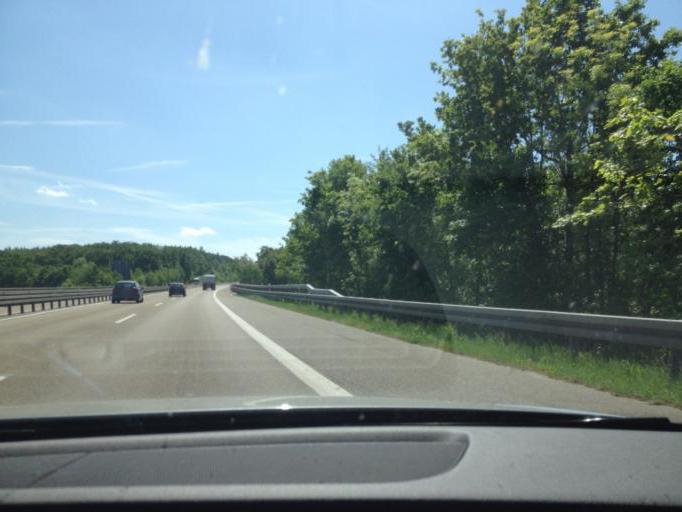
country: DE
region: North Rhine-Westphalia
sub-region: Regierungsbezirk Koln
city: Euskirchen
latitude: 50.6413
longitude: 6.7217
